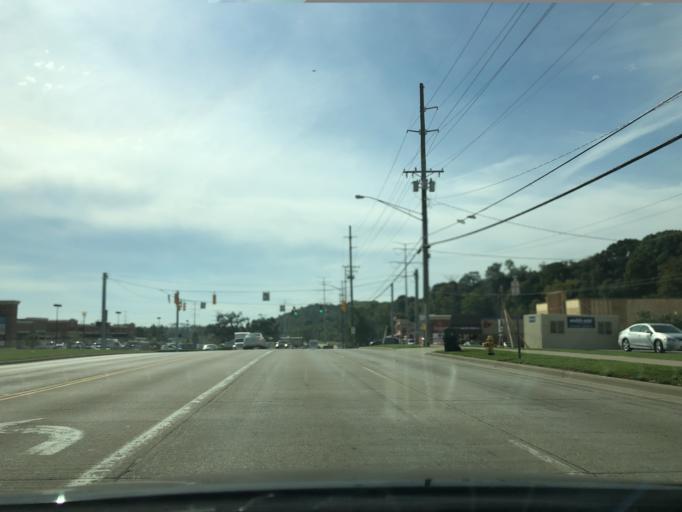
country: US
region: Ohio
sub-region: Hamilton County
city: Fairfax
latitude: 39.1479
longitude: -84.4047
